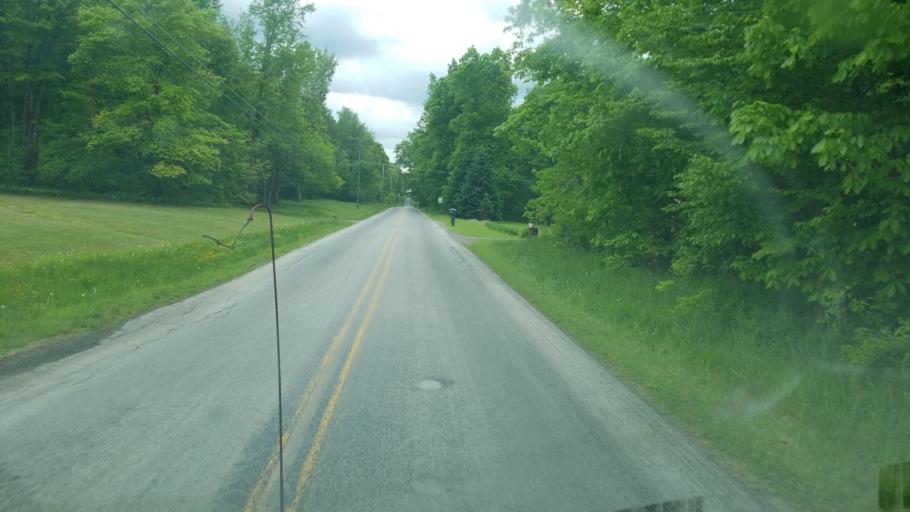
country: US
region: Pennsylvania
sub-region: Venango County
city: Franklin
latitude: 41.2122
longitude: -79.8450
